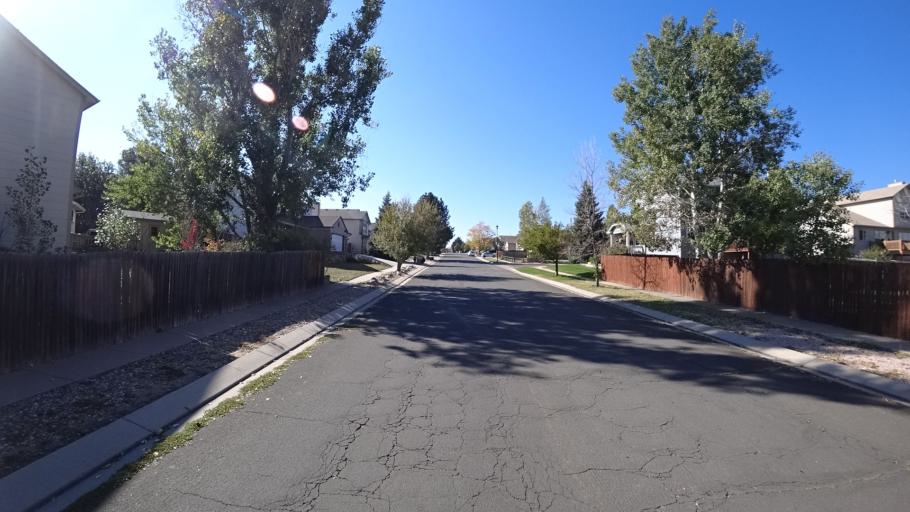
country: US
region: Colorado
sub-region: El Paso County
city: Cimarron Hills
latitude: 38.8841
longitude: -104.7047
